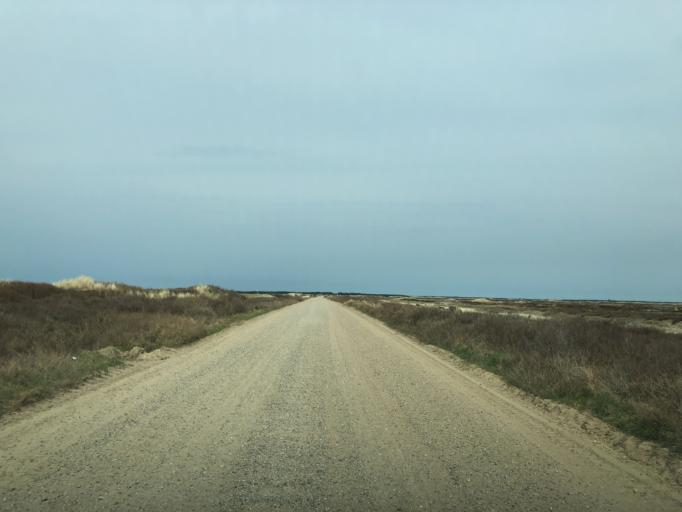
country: DK
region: South Denmark
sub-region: Varde Kommune
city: Oksbol
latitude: 55.5747
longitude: 8.1400
